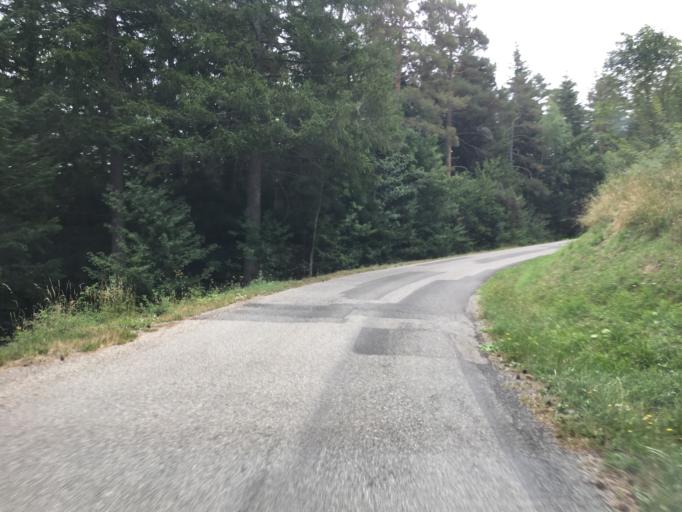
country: FR
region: Provence-Alpes-Cote d'Azur
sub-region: Departement des Alpes-de-Haute-Provence
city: Digne-les-Bains
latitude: 44.2183
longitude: 6.1418
